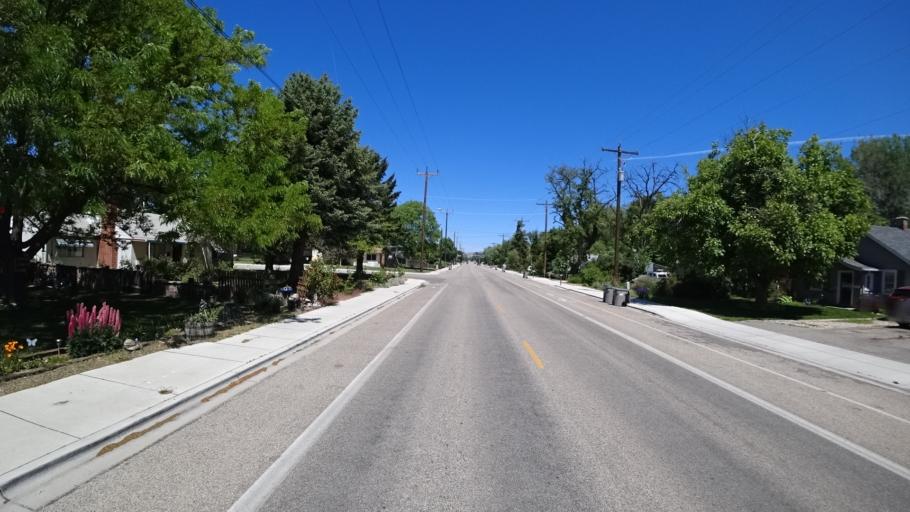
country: US
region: Idaho
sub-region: Ada County
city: Garden City
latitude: 43.5912
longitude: -116.2336
